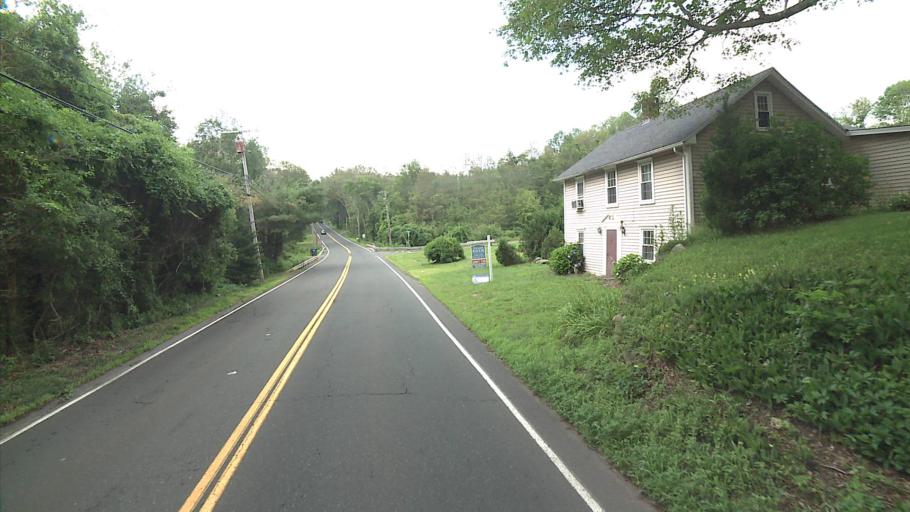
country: US
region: Connecticut
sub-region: Middlesex County
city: Higganum
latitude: 41.4524
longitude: -72.5552
